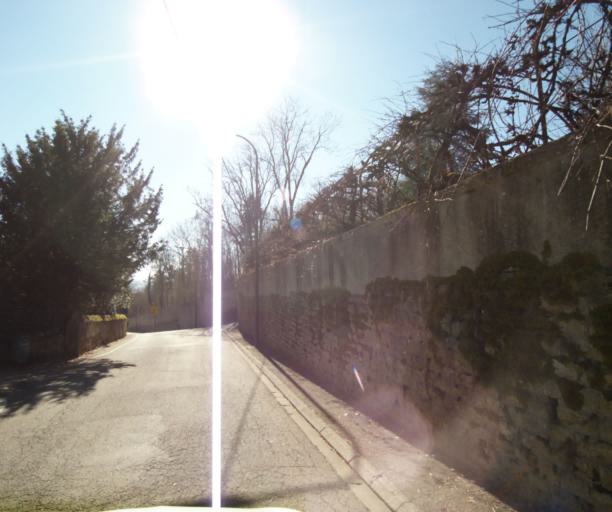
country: FR
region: Lorraine
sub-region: Departement de Meurthe-et-Moselle
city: Saint-Max
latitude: 48.7113
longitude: 6.2144
